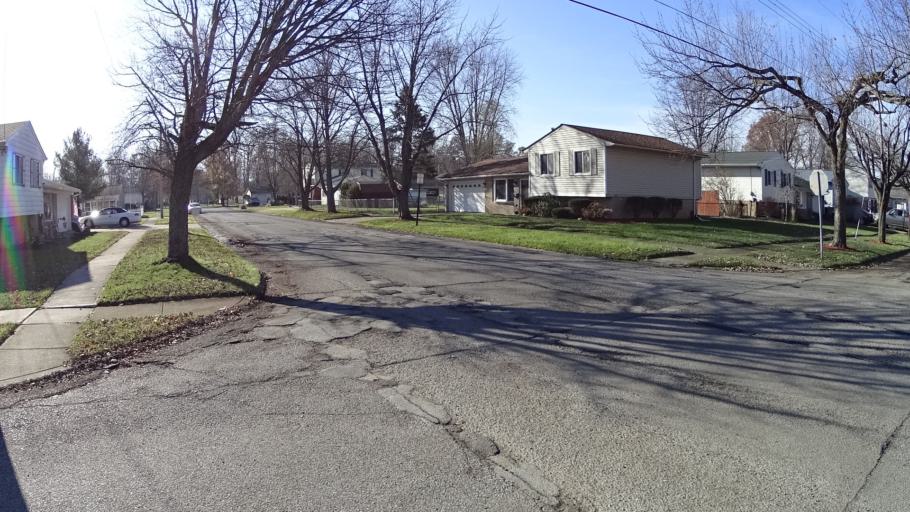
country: US
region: Ohio
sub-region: Lorain County
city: Sheffield
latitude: 41.3957
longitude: -82.0716
